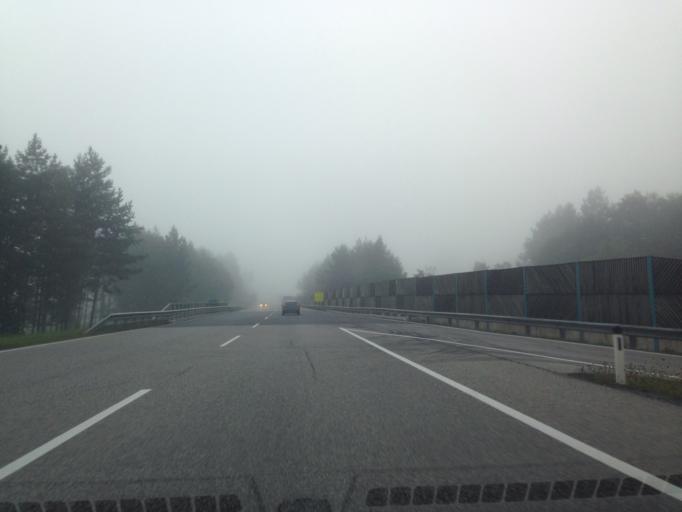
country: AT
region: Tyrol
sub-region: Politischer Bezirk Reutte
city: Lermoos
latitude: 47.4084
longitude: 10.8646
